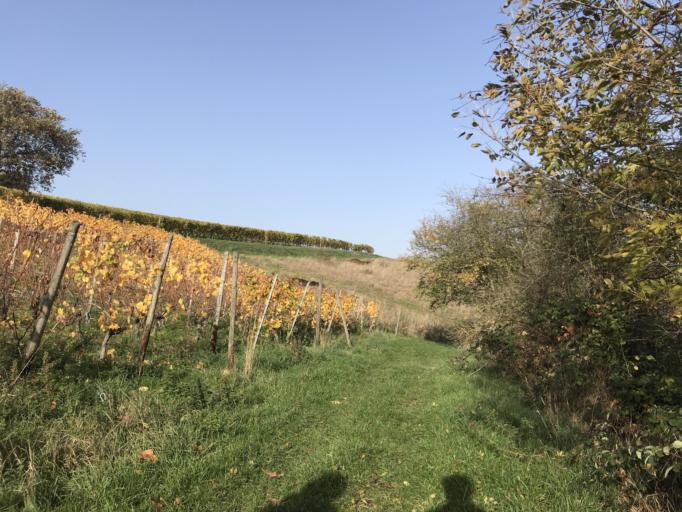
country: DE
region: Rheinland-Pfalz
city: Bacharach
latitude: 50.0629
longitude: 7.7647
